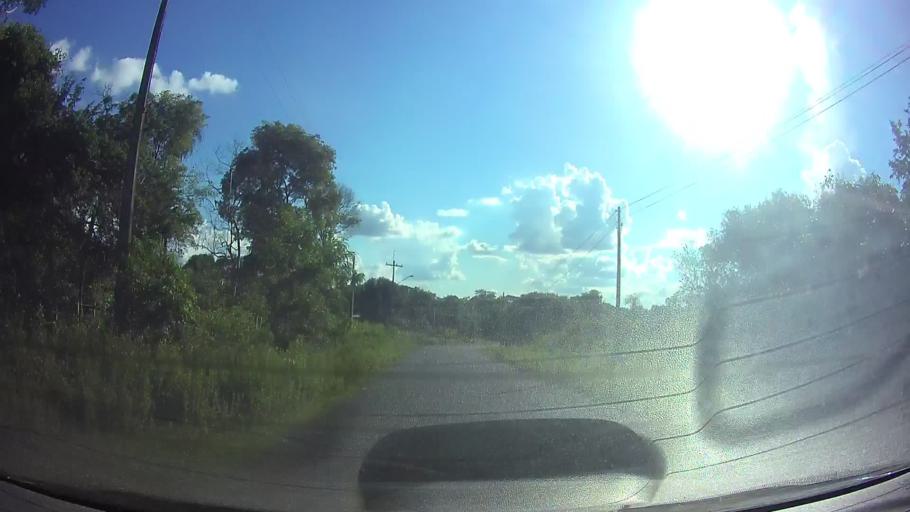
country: PY
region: Central
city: Aregua
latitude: -25.3334
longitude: -57.3787
